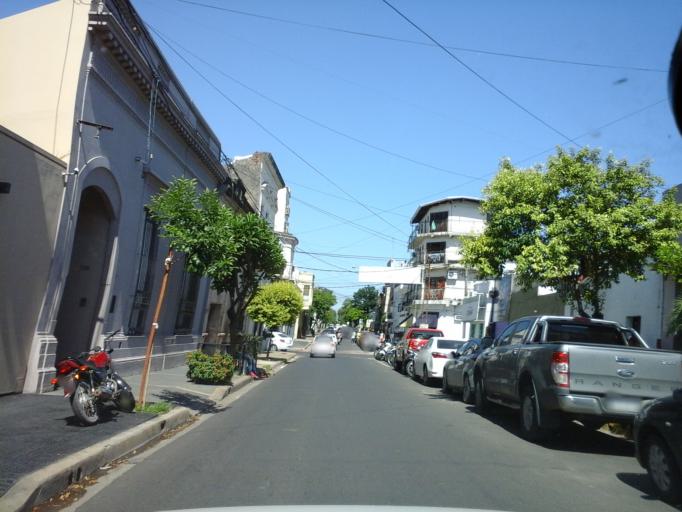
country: AR
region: Corrientes
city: Corrientes
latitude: -27.4633
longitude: -58.8334
